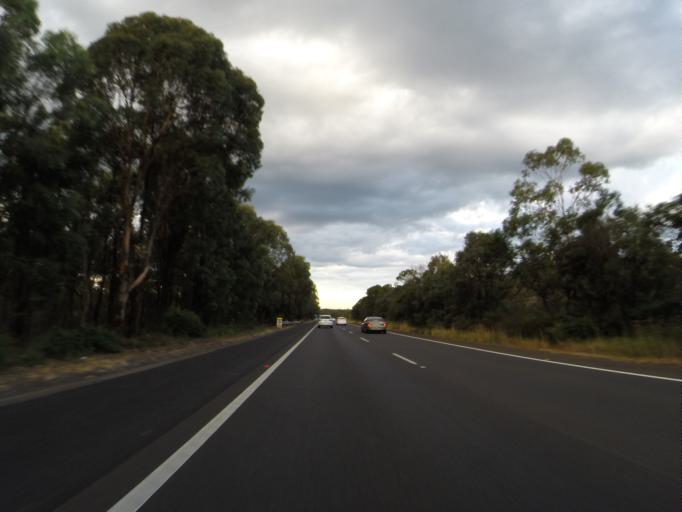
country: AU
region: New South Wales
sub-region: Wollondilly
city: Buxton
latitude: -34.2946
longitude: 150.6206
